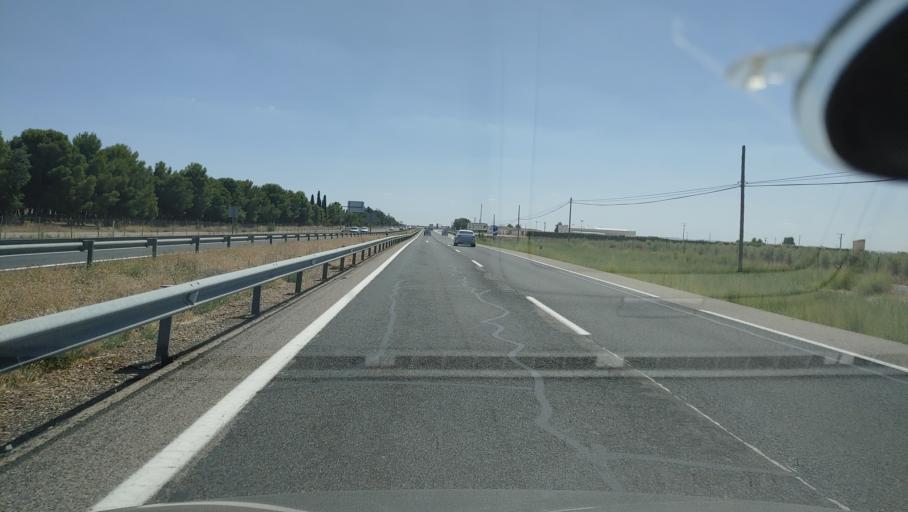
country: ES
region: Castille-La Mancha
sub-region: Provincia de Ciudad Real
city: Manzanares
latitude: 39.1173
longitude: -3.3775
